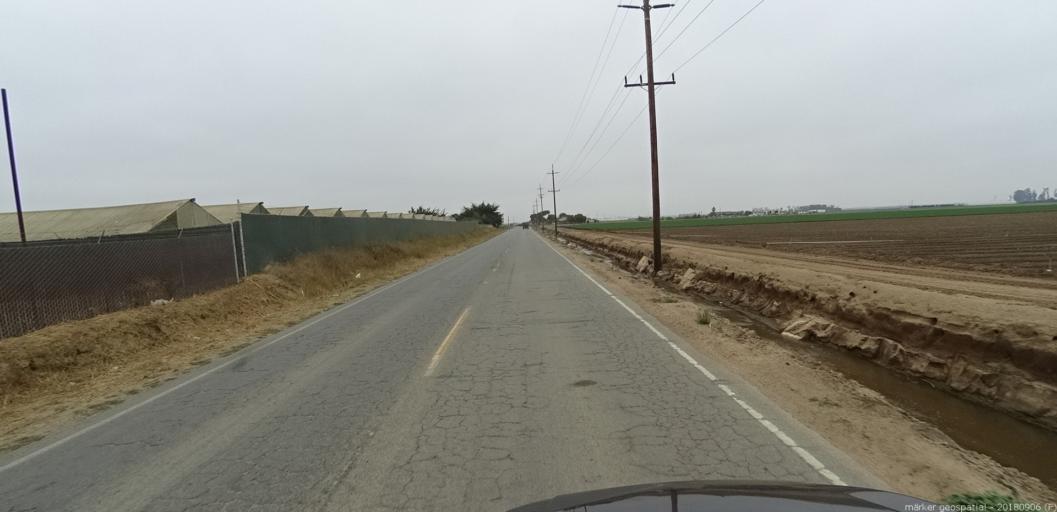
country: US
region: California
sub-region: Monterey County
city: Chualar
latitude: 36.6381
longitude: -121.5636
